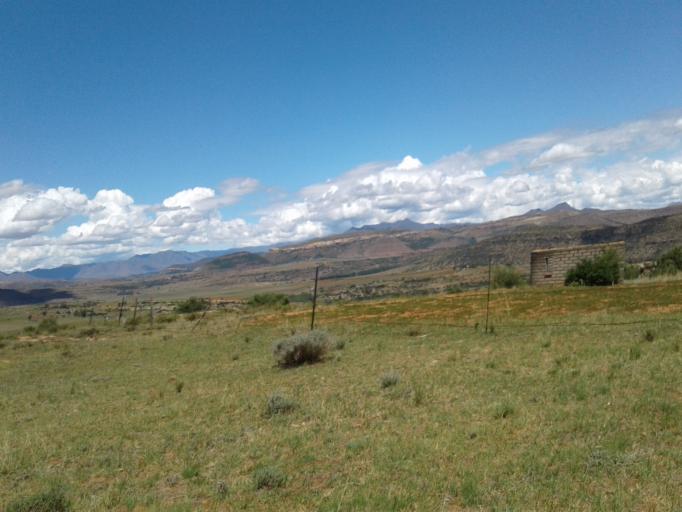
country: LS
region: Quthing
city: Quthing
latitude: -30.3821
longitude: 27.5585
